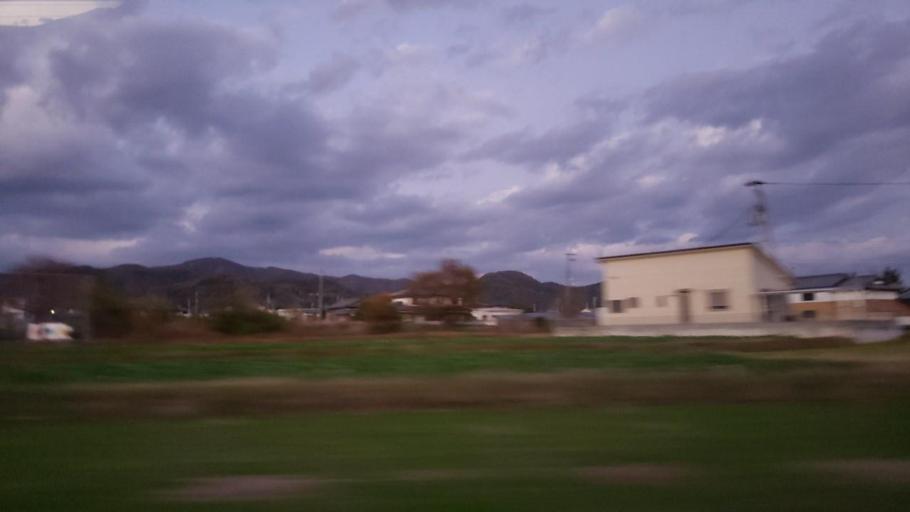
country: JP
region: Tokushima
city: Kamojimacho-jogejima
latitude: 34.0900
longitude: 134.2865
